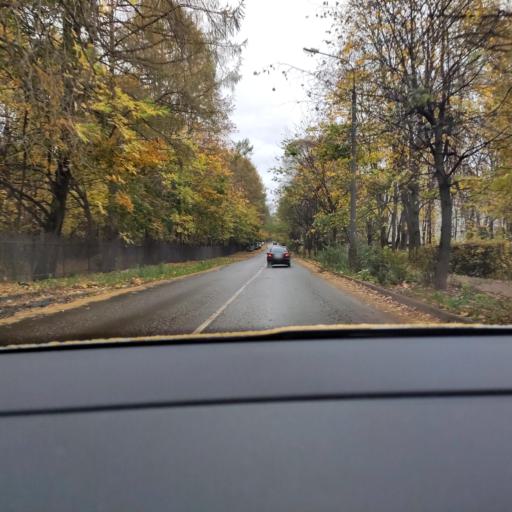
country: RU
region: Moskovskaya
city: Ivanteyevka
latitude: 55.9731
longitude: 37.8989
